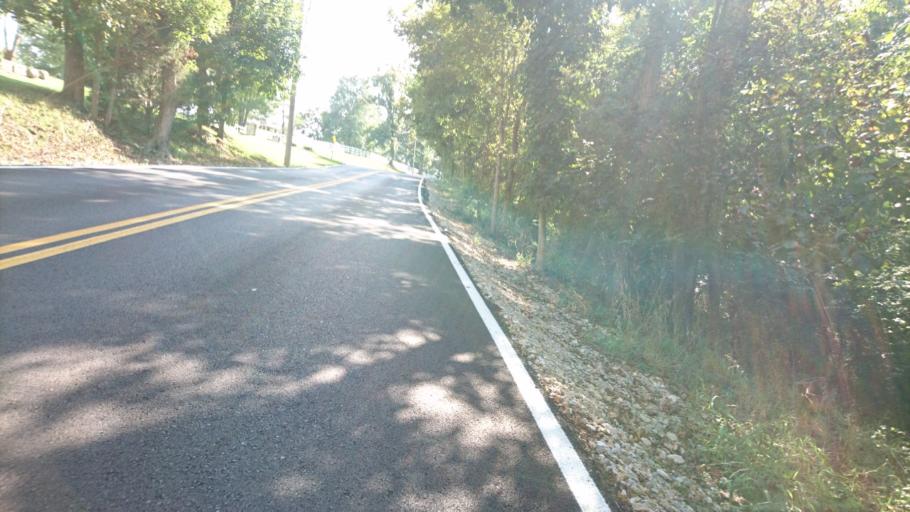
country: US
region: Missouri
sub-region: Saint Louis County
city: Eureka
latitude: 38.5397
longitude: -90.6355
